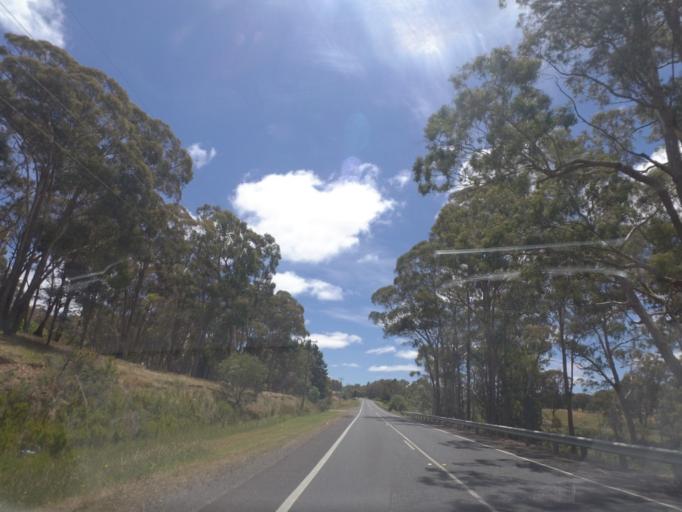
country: AU
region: Victoria
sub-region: Mount Alexander
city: Castlemaine
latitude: -37.2882
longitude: 144.1627
